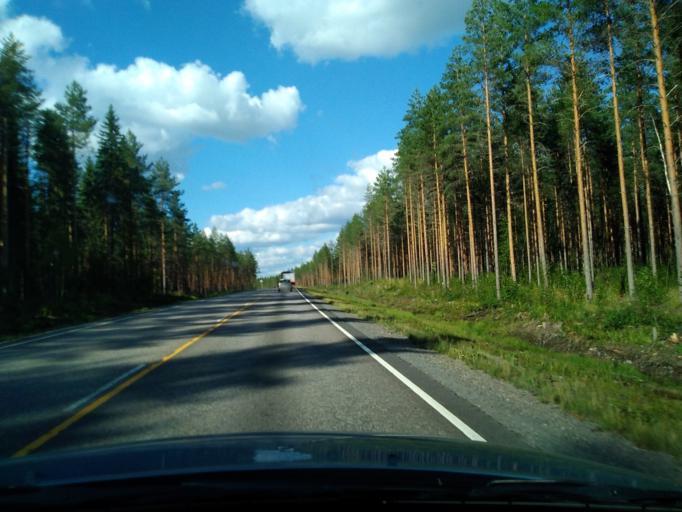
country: FI
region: Central Finland
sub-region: Keuruu
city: Keuruu
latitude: 62.1456
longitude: 24.7467
